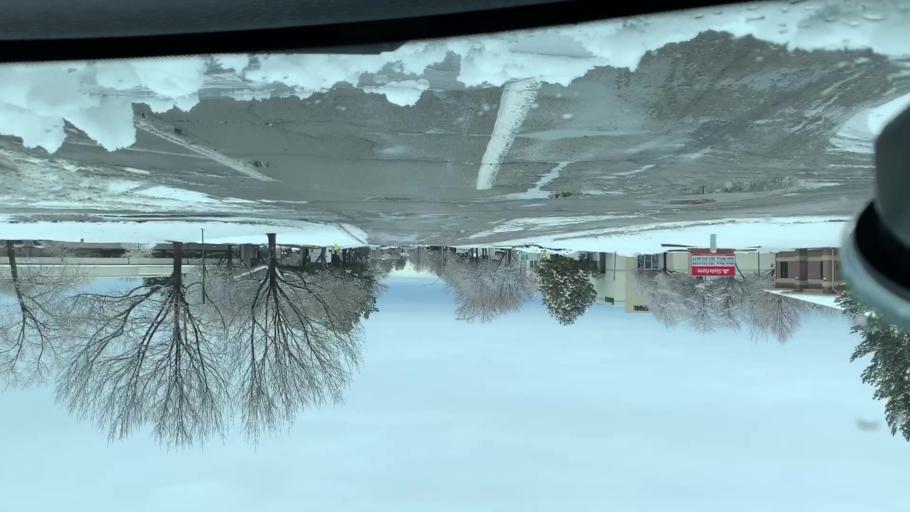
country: US
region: Colorado
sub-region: Adams County
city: Northglenn
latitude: 39.9152
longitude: -104.9819
